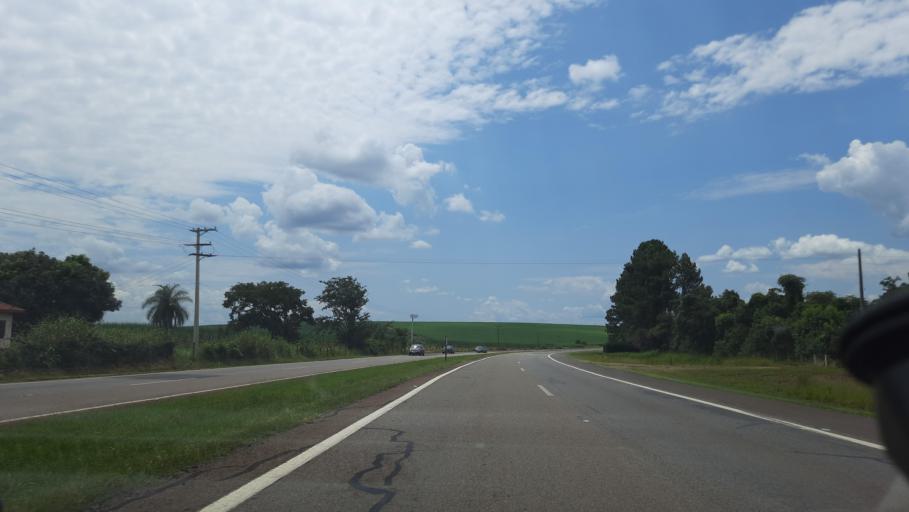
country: BR
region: Sao Paulo
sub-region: Casa Branca
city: Casa Branca
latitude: -21.7042
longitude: -47.0854
